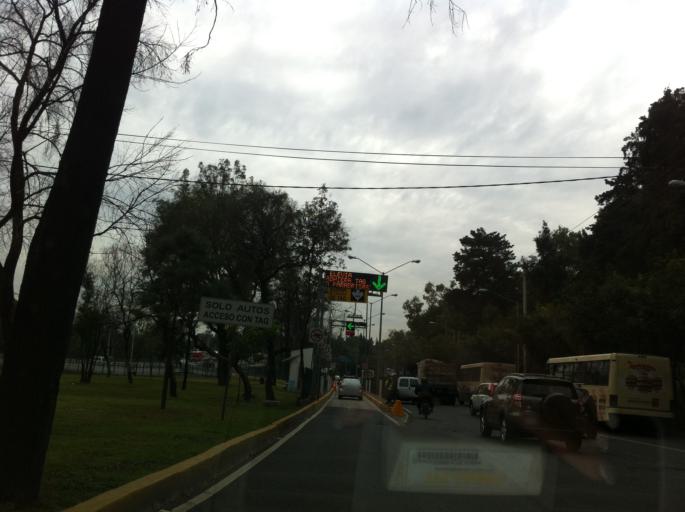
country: MX
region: Mexico City
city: Polanco
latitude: 19.4246
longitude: -99.2009
